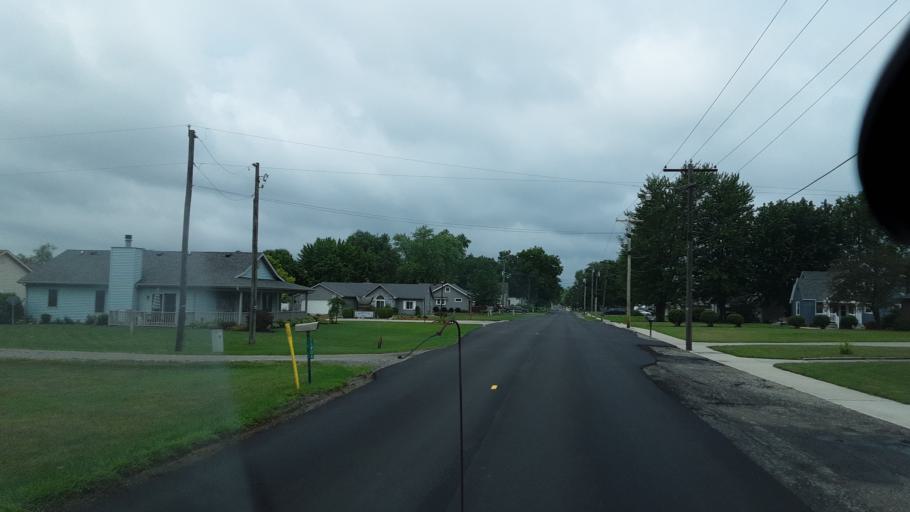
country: US
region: Indiana
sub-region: Allen County
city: Monroeville
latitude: 40.9483
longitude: -84.9840
